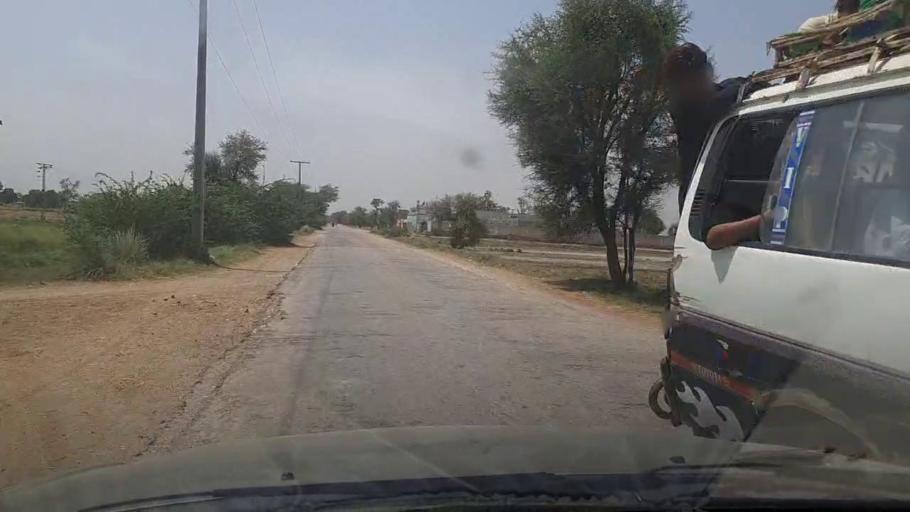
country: PK
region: Sindh
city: Bhiria
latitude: 26.8974
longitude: 68.2273
